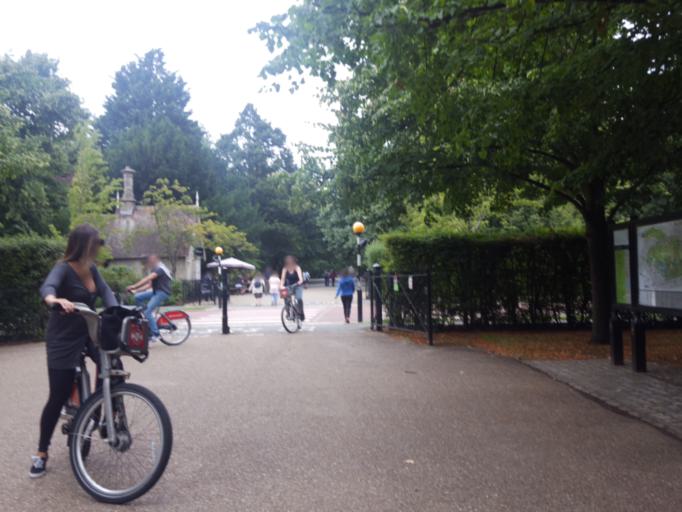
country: GB
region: England
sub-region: Greater London
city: Camden Town
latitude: 51.5283
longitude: -0.1485
